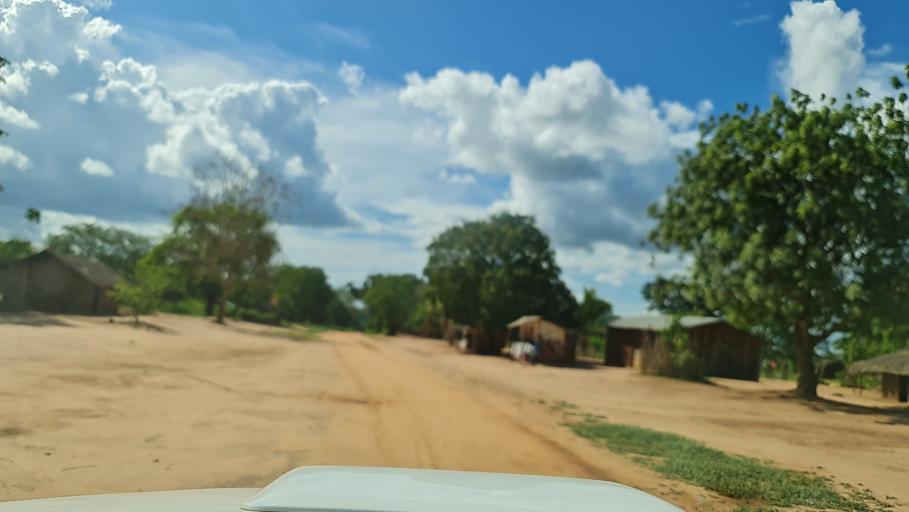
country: MZ
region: Nampula
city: Ilha de Mocambique
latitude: -15.4192
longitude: 40.2646
